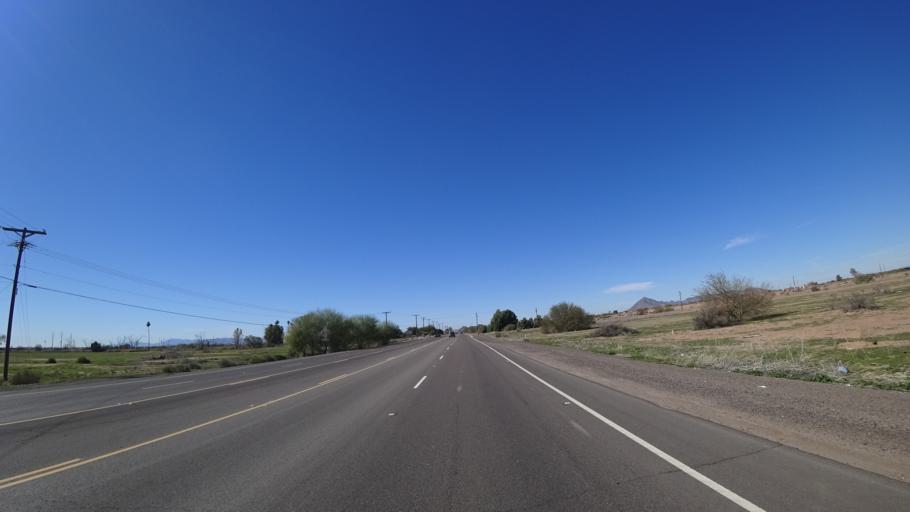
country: US
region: Arizona
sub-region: Maricopa County
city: Mesa
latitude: 33.4661
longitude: -111.8461
